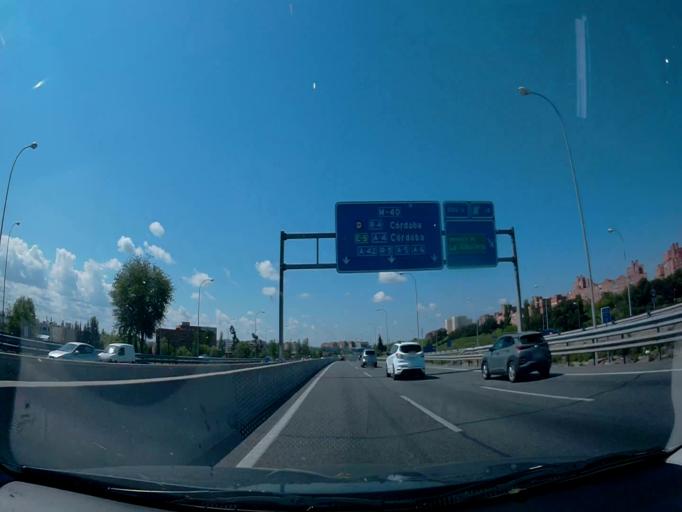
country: ES
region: Madrid
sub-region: Provincia de Madrid
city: Vicalvaro
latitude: 40.3919
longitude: -3.6303
